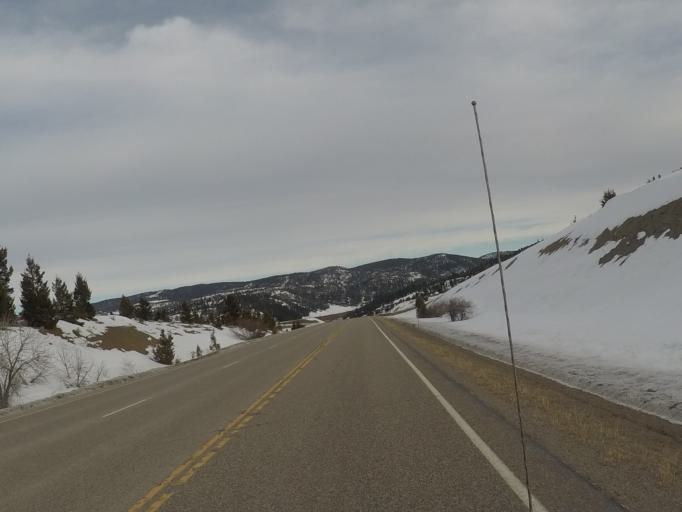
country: US
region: Montana
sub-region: Meagher County
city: White Sulphur Springs
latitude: 46.6587
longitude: -110.8733
